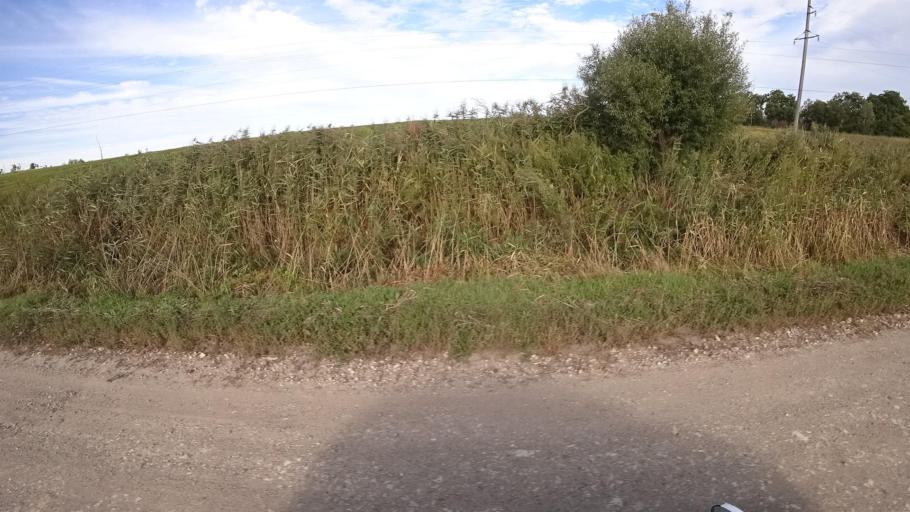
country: RU
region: Primorskiy
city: Dostoyevka
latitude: 44.3108
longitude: 133.4636
